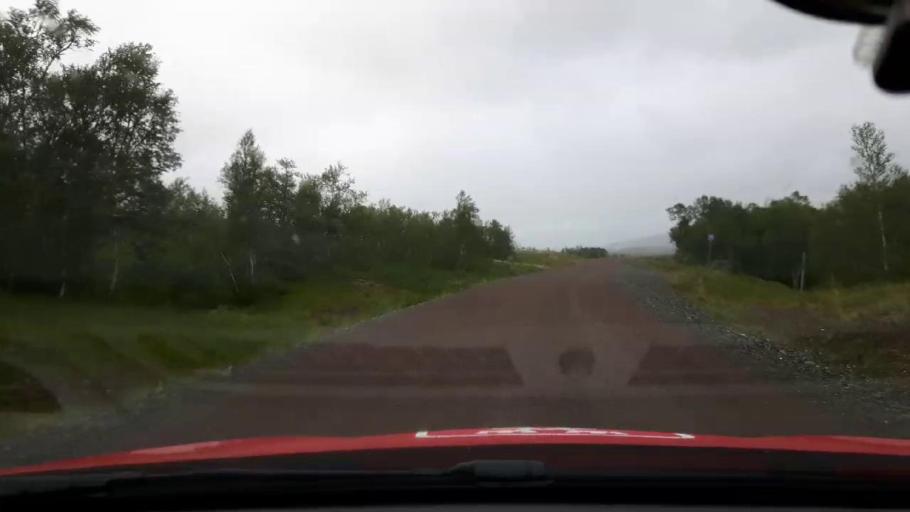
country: NO
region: Nord-Trondelag
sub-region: Meraker
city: Meraker
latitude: 63.1873
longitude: 12.3803
